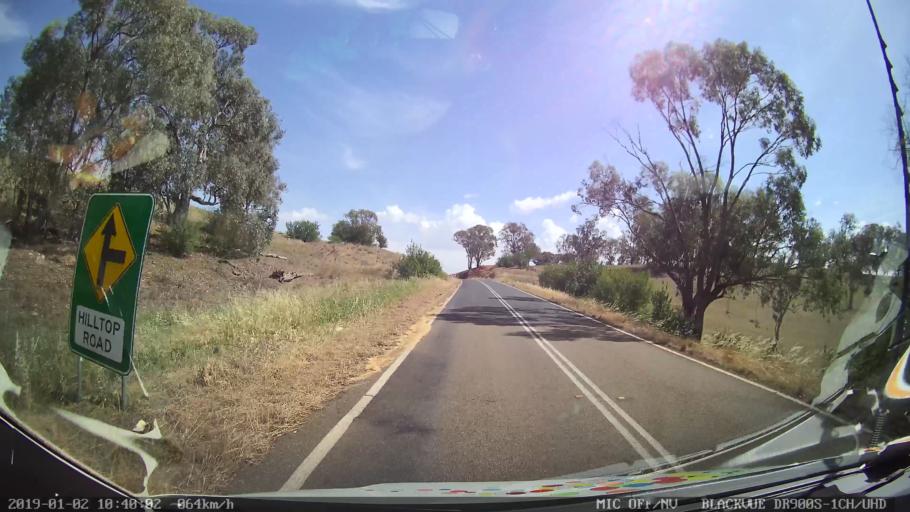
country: AU
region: New South Wales
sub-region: Cootamundra
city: Cootamundra
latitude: -34.8054
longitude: 148.3174
